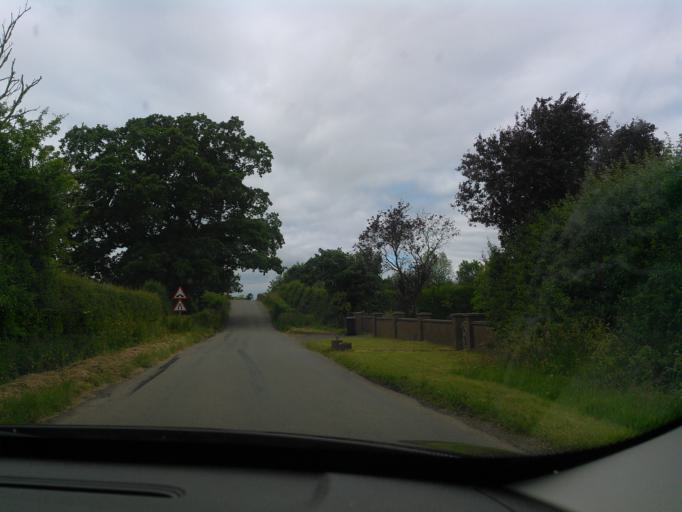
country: GB
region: England
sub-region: Shropshire
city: Wem
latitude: 52.9034
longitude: -2.7549
